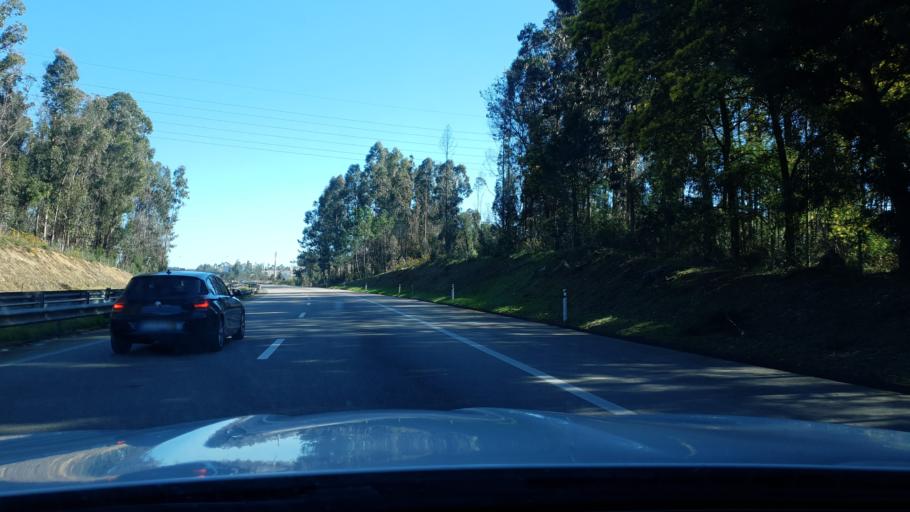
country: PT
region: Aveiro
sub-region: Santa Maria da Feira
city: Nogueira da Regedoura
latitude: 41.0084
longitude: -8.5986
